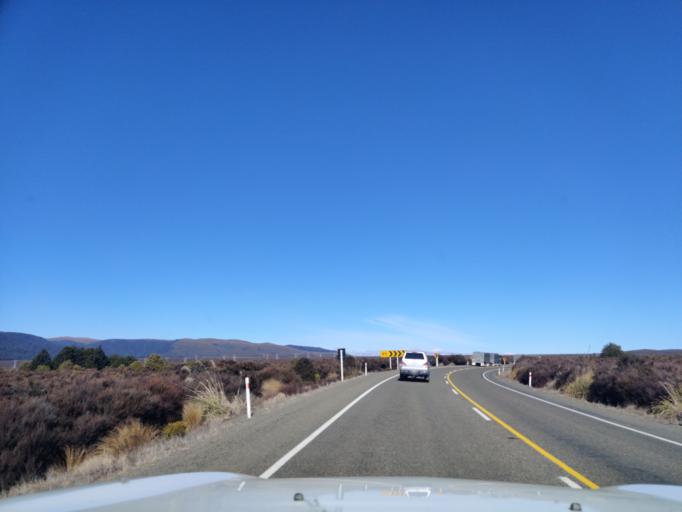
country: NZ
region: Waikato
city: Turangi
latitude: -39.2302
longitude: 175.7351
